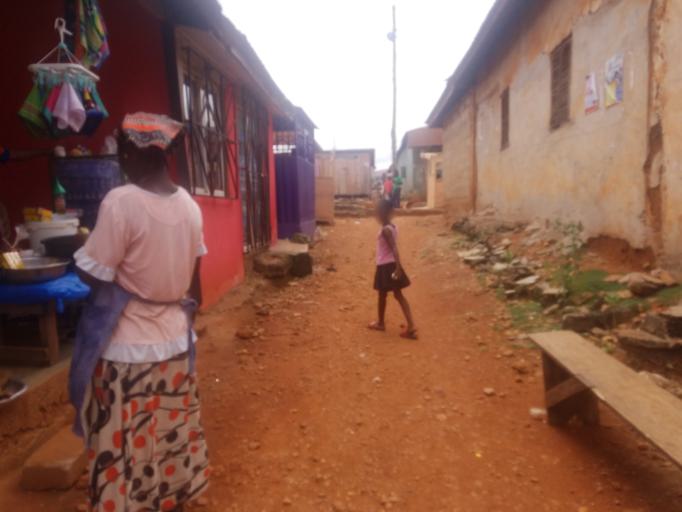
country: GH
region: Western
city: Bibiani
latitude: 6.8051
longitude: -2.5151
